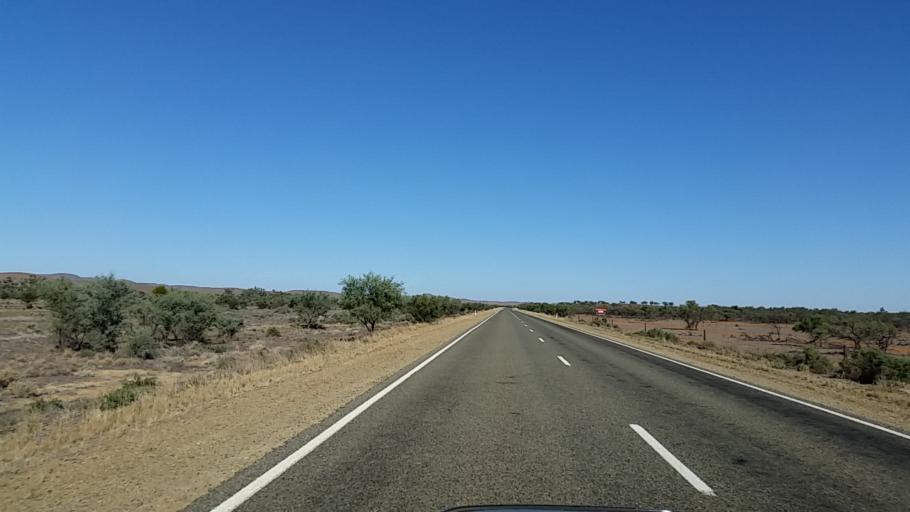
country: AU
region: South Australia
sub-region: Flinders Ranges
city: Quorn
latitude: -32.3897
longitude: 138.5059
